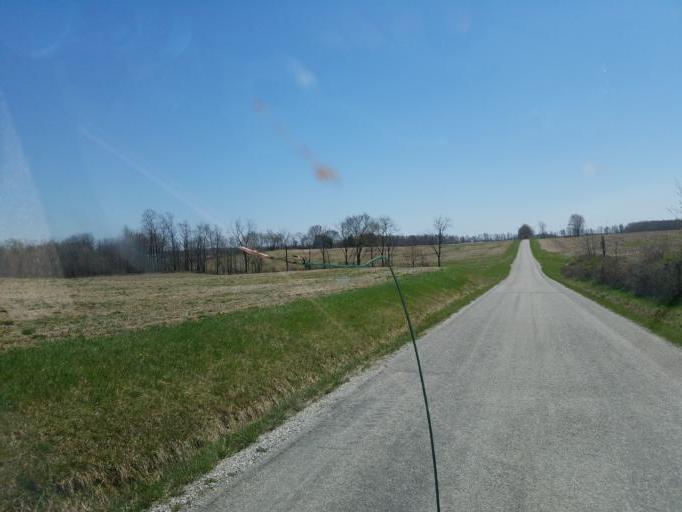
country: US
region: Ohio
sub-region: Huron County
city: Greenwich
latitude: 40.9798
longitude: -82.4568
